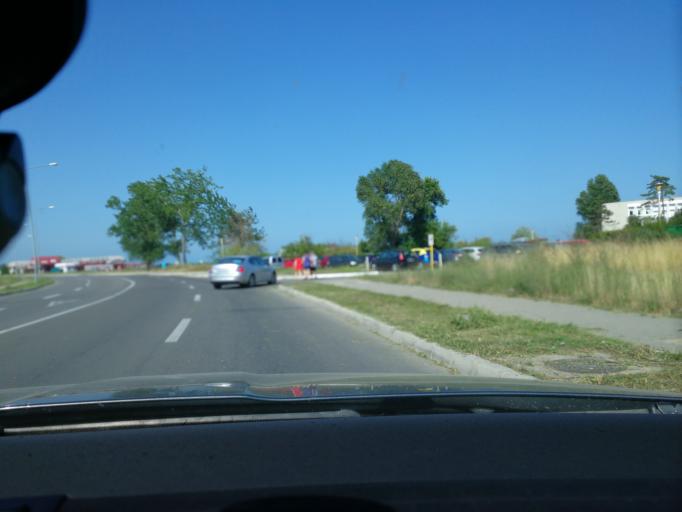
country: RO
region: Constanta
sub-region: Municipiul Mangalia
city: Mangalia
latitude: 43.8313
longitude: 28.5872
